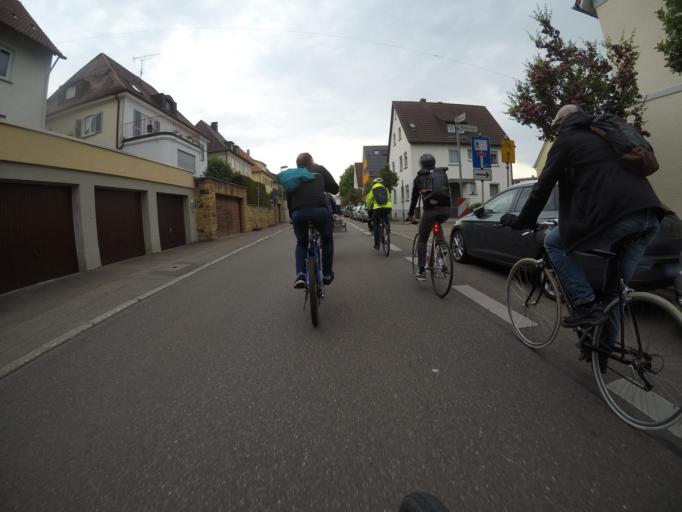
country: DE
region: Baden-Wuerttemberg
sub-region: Regierungsbezirk Stuttgart
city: Esslingen
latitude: 48.7382
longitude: 9.3223
